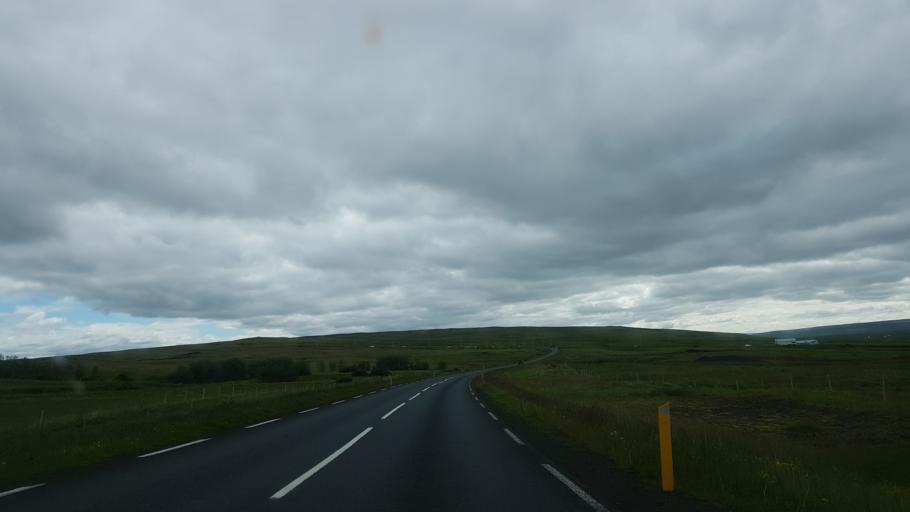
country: IS
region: Northwest
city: Saudarkrokur
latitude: 65.3600
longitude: -20.8908
